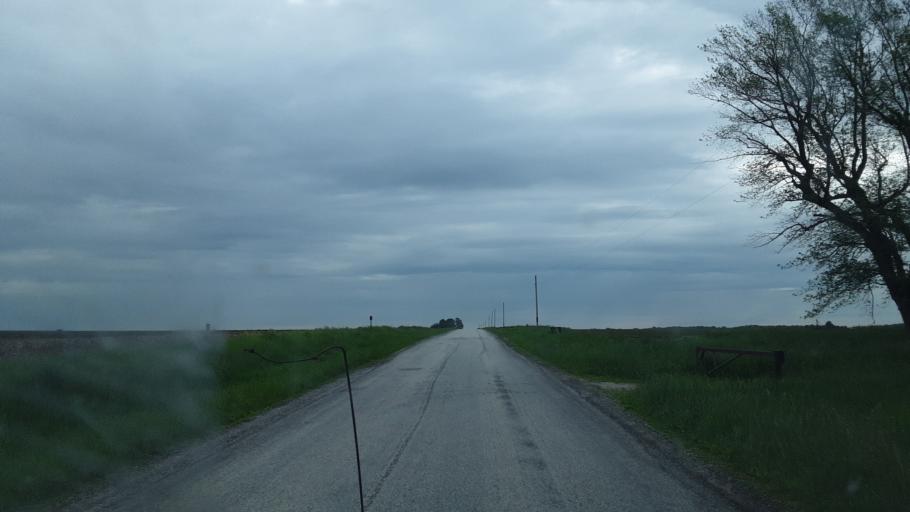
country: US
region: Illinois
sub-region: McDonough County
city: Macomb
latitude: 40.3818
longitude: -90.6422
